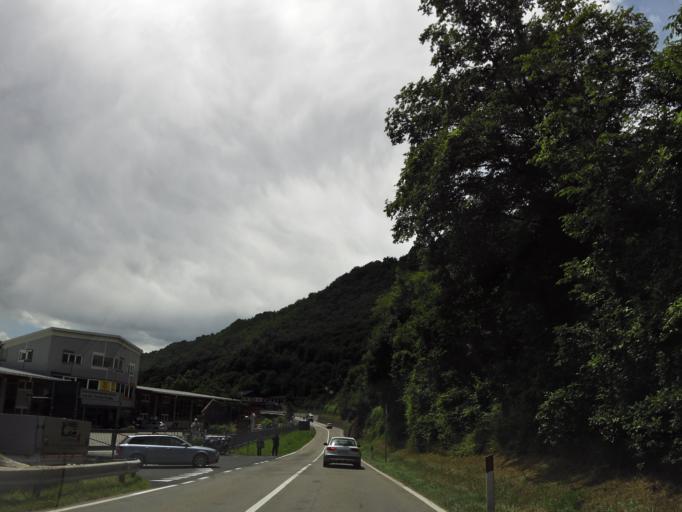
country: IT
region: Trentino-Alto Adige
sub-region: Bolzano
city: Villandro - Villanders
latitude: 46.6139
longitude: 11.5358
